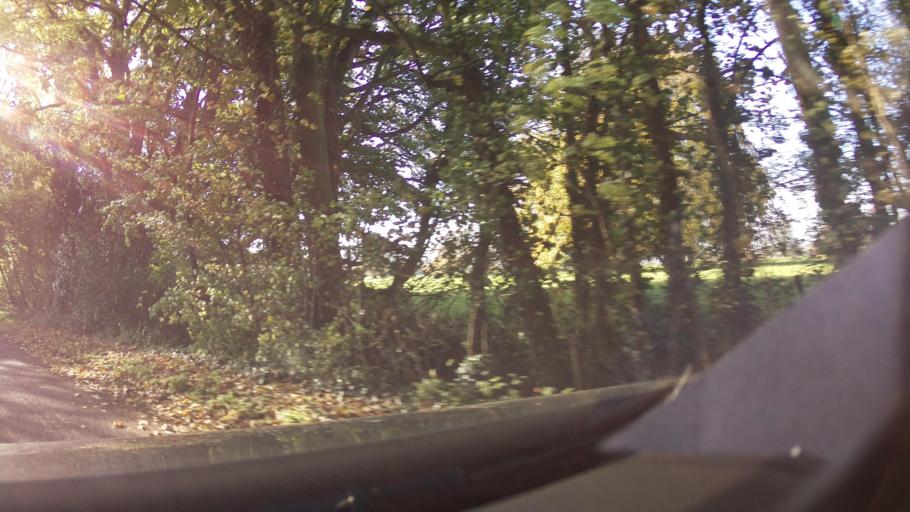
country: GB
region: England
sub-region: Somerset
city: Castle Cary
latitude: 51.0561
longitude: -2.4824
